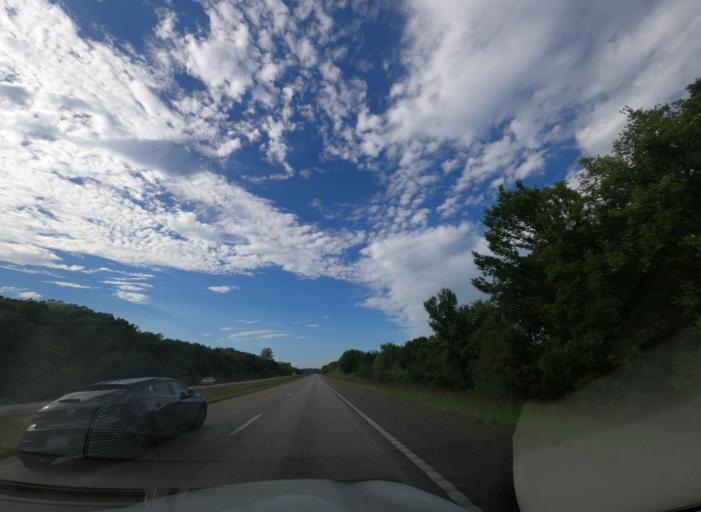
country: US
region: Missouri
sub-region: Jefferson County
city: Crystal City
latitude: 38.0771
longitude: -90.2942
